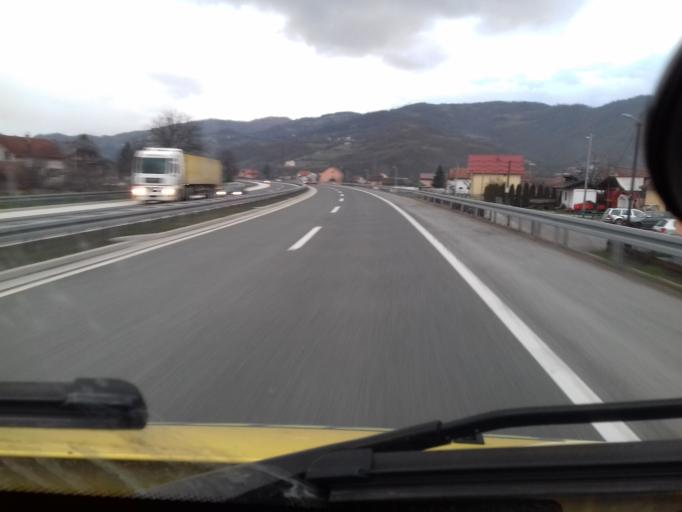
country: BA
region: Federation of Bosnia and Herzegovina
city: Ilijas
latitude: 43.9471
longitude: 18.2558
